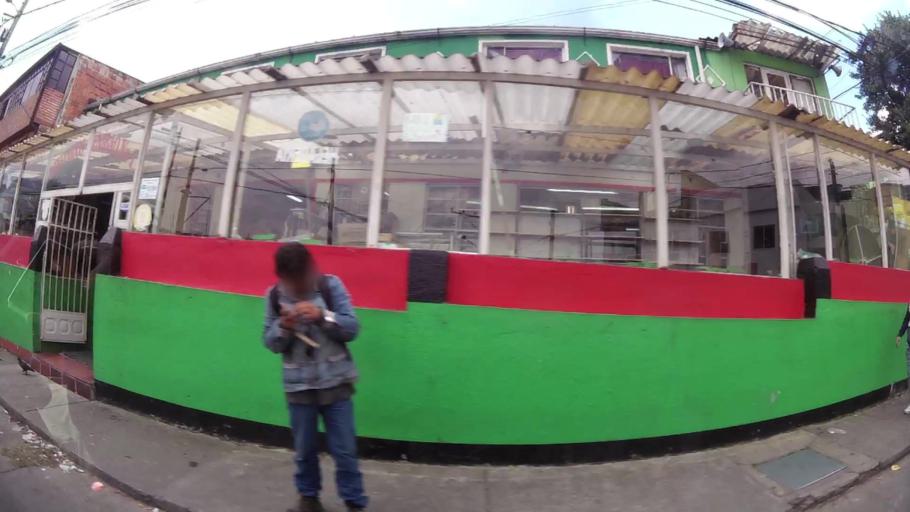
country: CO
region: Bogota D.C.
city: Bogota
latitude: 4.5857
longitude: -74.0674
